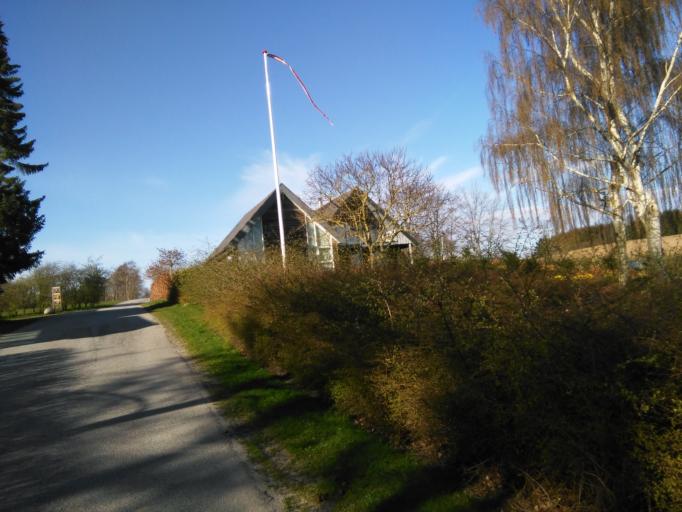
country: DK
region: Central Jutland
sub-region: Arhus Kommune
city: Malling
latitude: 56.0339
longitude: 10.2154
